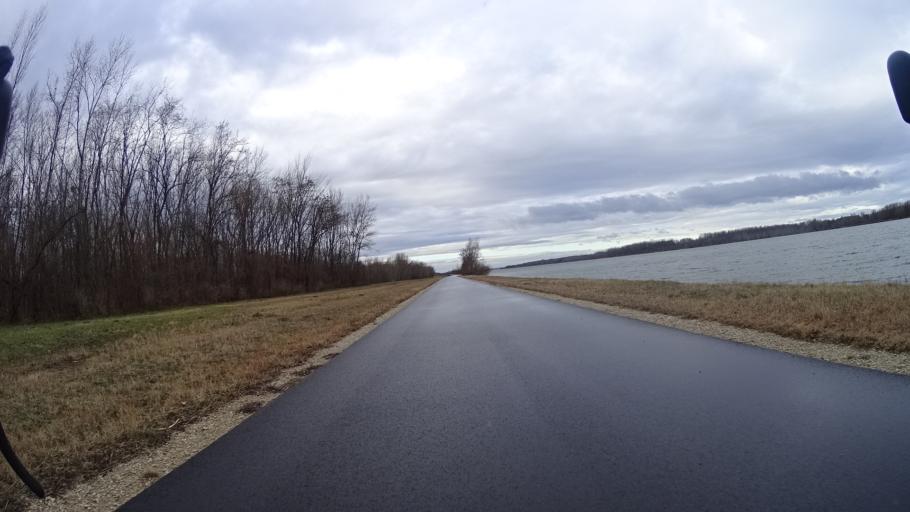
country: AT
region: Lower Austria
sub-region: Politischer Bezirk Tulln
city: Wordern
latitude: 48.3460
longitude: 16.2035
